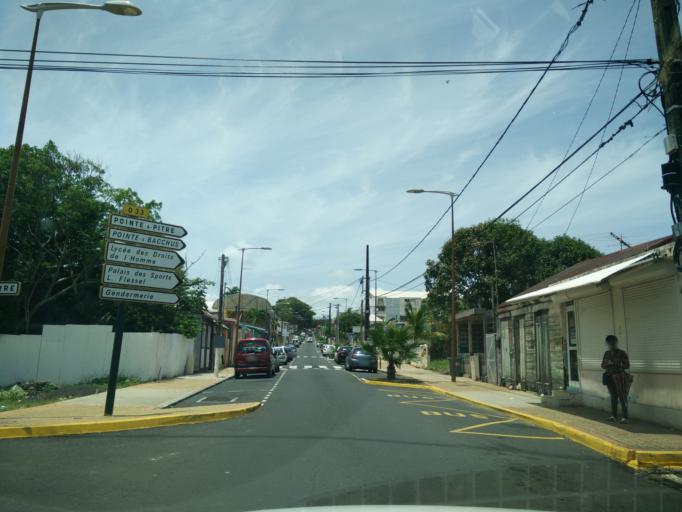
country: GP
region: Guadeloupe
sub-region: Guadeloupe
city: Petit-Bourg
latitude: 16.1936
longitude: -61.5919
